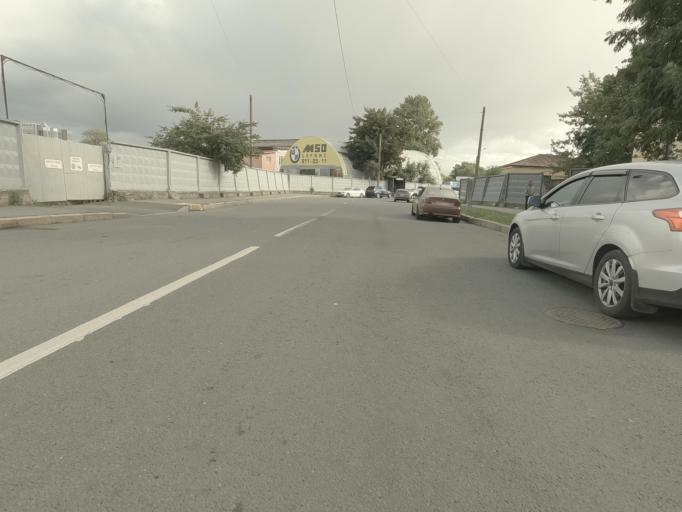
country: RU
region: St.-Petersburg
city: Centralniy
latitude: 59.9235
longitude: 30.3767
